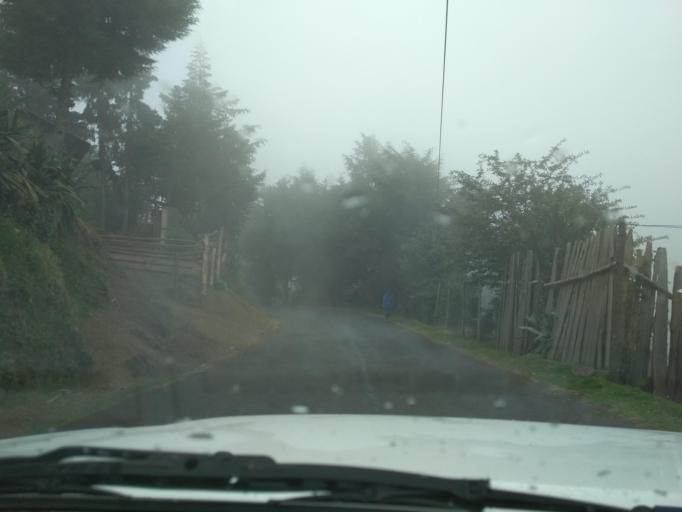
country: MX
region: Veracruz
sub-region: Mariano Escobedo
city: San Isidro el Berro
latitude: 18.9301
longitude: -97.2151
